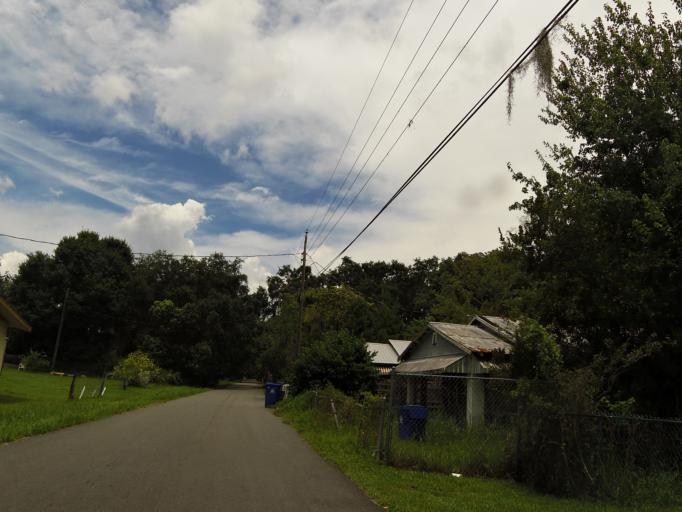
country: US
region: Florida
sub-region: Putnam County
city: East Palatka
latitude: 29.7217
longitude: -81.5087
